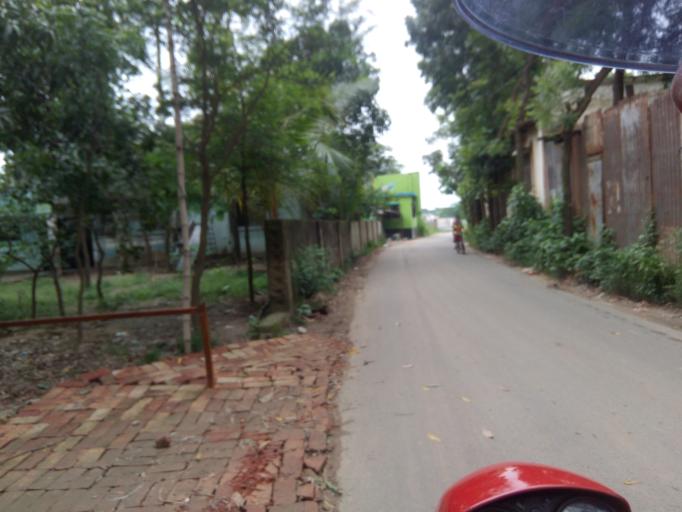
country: BD
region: Dhaka
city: Azimpur
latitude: 23.7430
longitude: 90.3375
